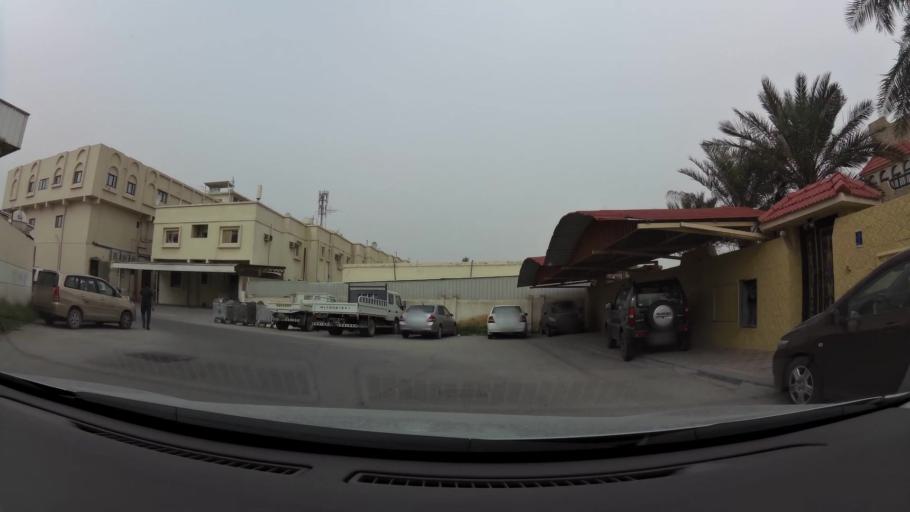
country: QA
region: Baladiyat ad Dawhah
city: Doha
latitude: 25.2602
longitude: 51.4923
